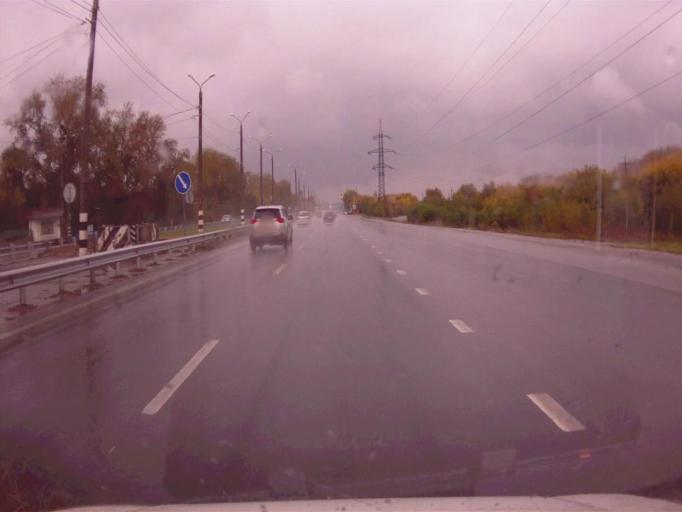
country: RU
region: Chelyabinsk
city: Dolgoderevenskoye
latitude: 55.2554
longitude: 61.3527
